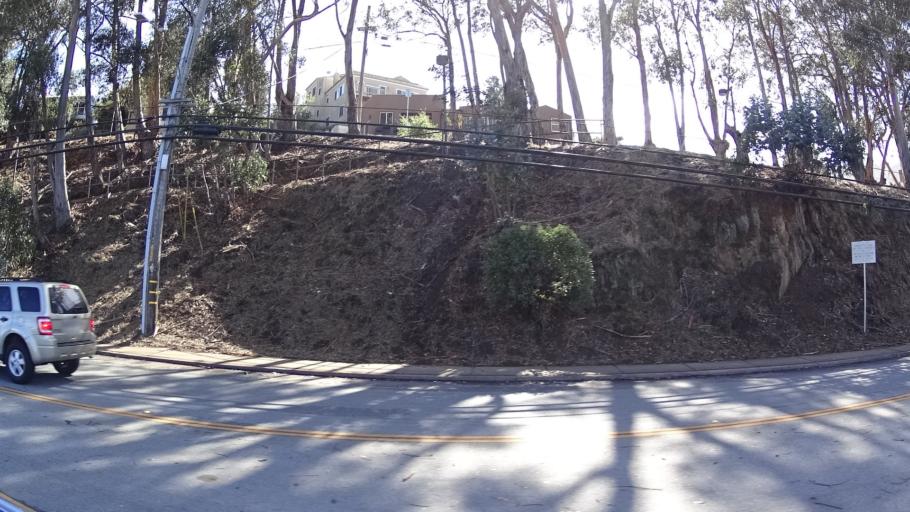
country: US
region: California
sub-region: San Mateo County
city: Brisbane
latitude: 37.6851
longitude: -122.3992
